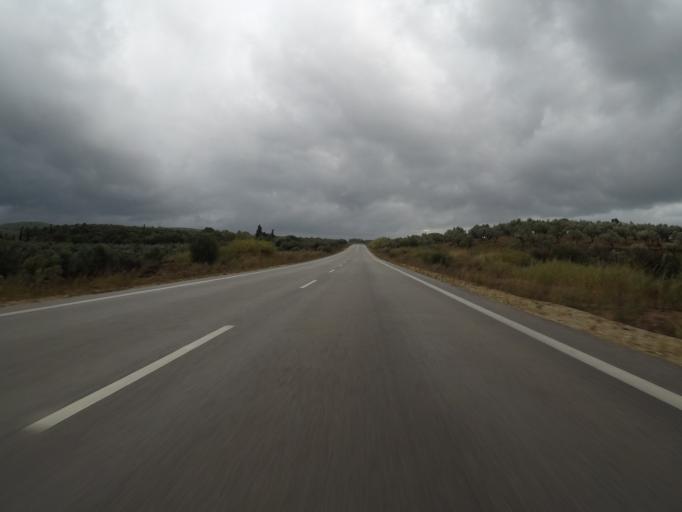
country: GR
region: Peloponnese
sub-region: Nomos Messinias
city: Gargalianoi
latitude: 37.0132
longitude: 21.6506
